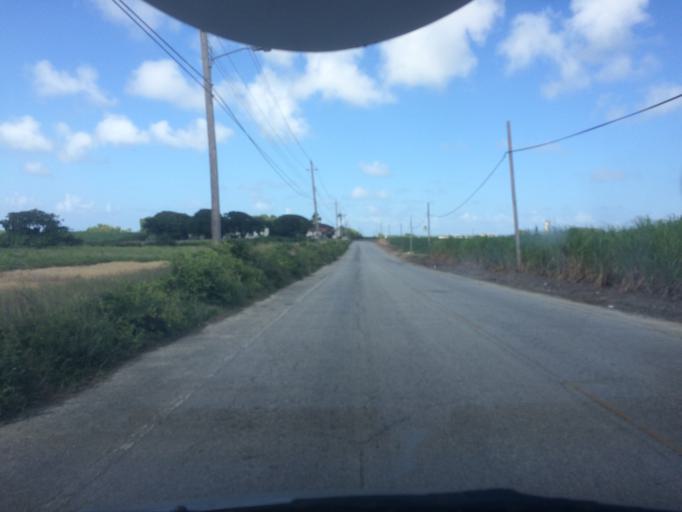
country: BB
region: Saint Lucy
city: Checker Hall
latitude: 13.2876
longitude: -59.6228
